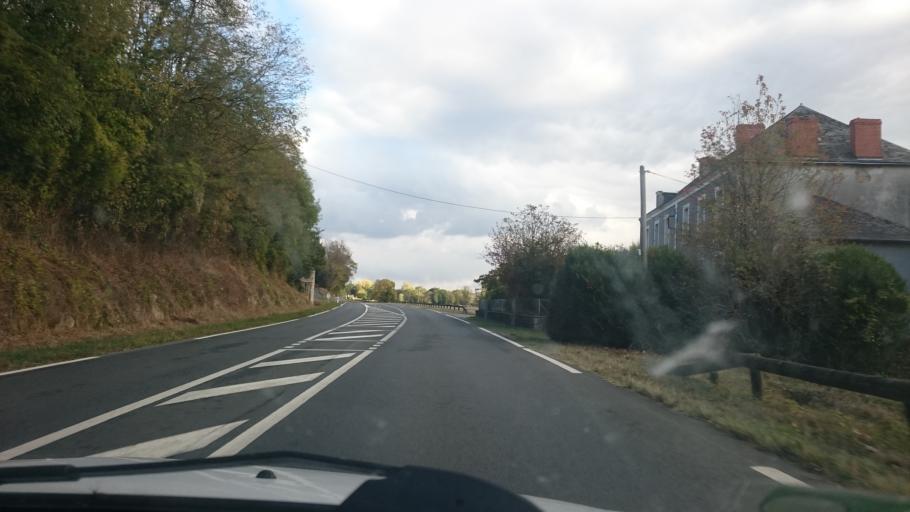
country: FR
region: Centre
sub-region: Departement de l'Indre
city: Saint-Gaultier
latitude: 46.6330
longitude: 1.4568
